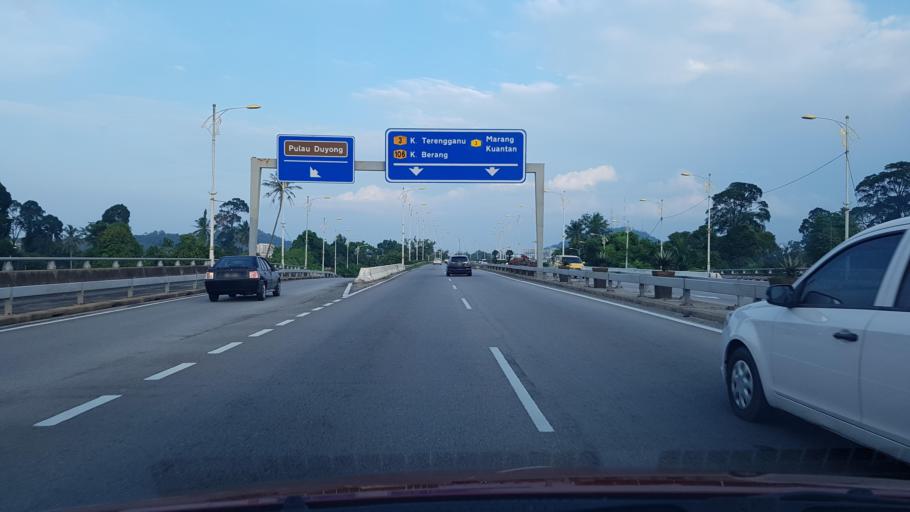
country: MY
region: Terengganu
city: Kuala Terengganu
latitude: 5.3307
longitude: 103.1202
